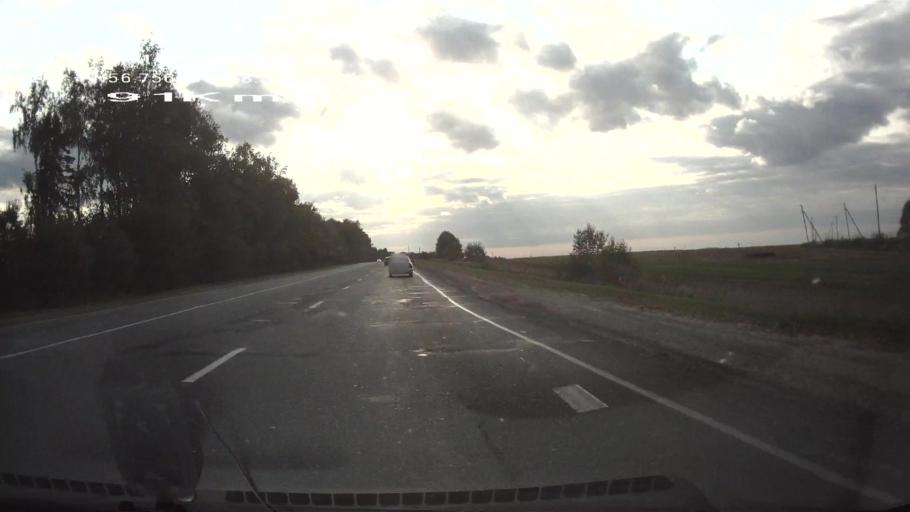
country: RU
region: Mariy-El
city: Sovetskiy
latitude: 56.7565
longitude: 48.5268
